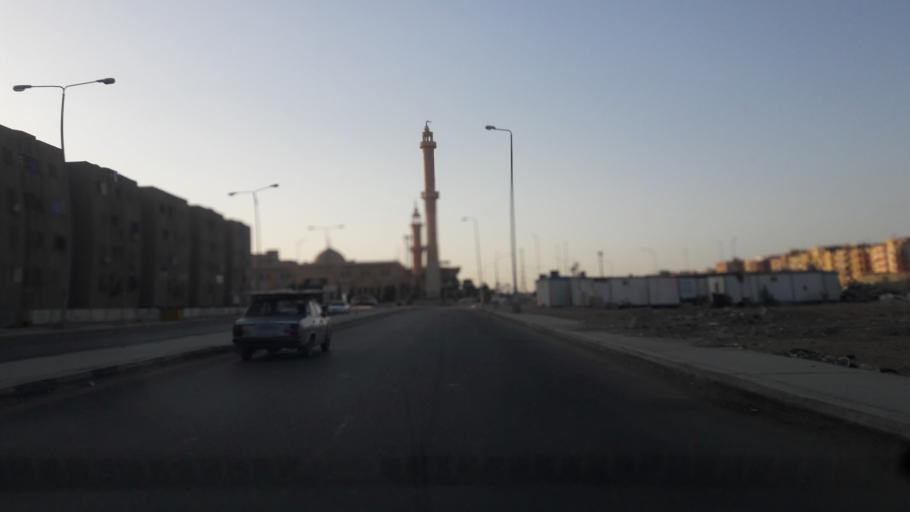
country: EG
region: Al Jizah
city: Madinat Sittah Uktubar
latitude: 29.9513
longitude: 30.9366
